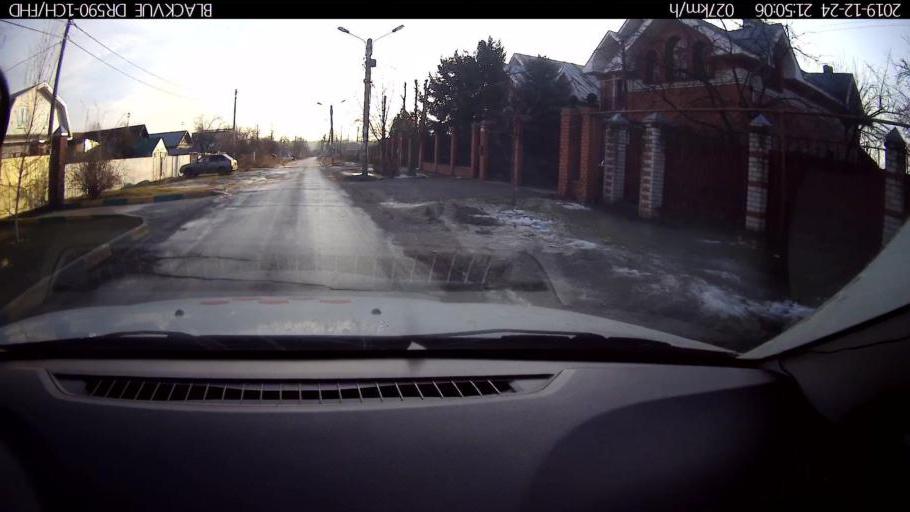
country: RU
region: Nizjnij Novgorod
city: Burevestnik
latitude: 56.2226
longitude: 43.8442
